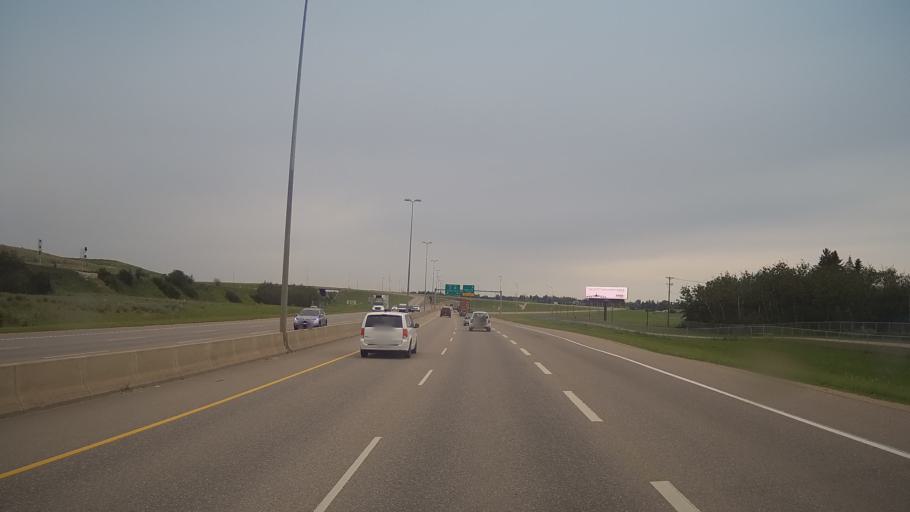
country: CA
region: Saskatchewan
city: Saskatoon
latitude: 52.1020
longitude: -106.7039
